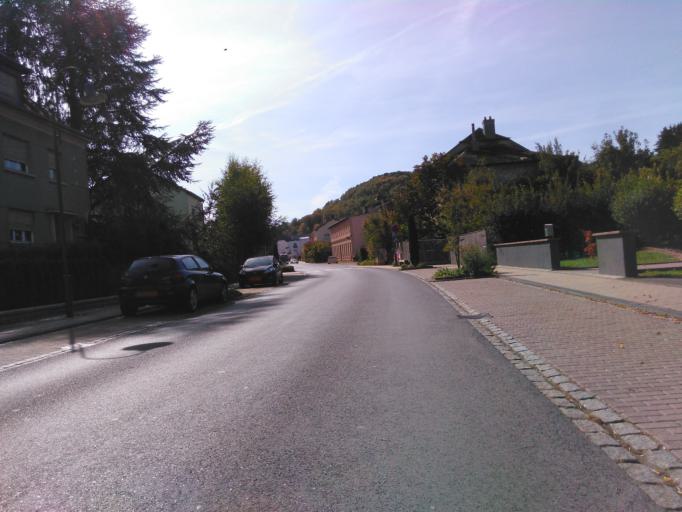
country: LU
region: Luxembourg
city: Tetange
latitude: 49.4789
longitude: 6.0364
